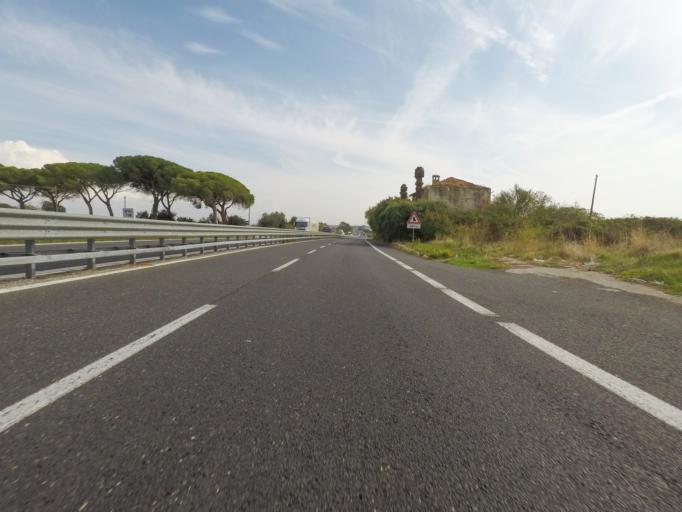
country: IT
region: Latium
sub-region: Provincia di Viterbo
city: Pescia Romana
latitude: 42.3895
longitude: 11.5420
